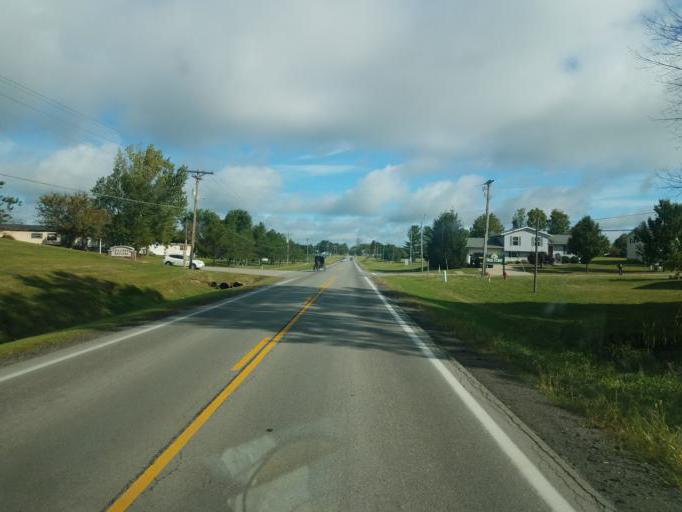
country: US
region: Ohio
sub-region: Wayne County
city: West Salem
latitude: 40.9607
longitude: -82.1095
